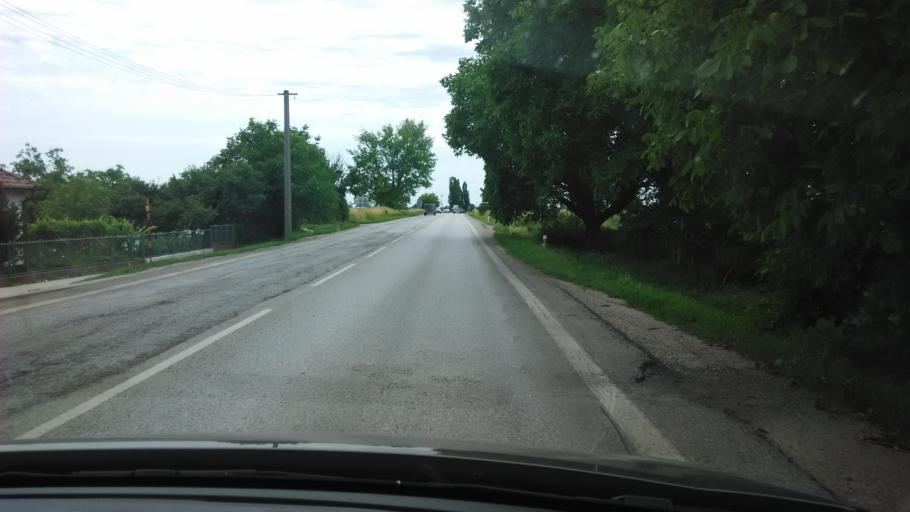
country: SK
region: Trnavsky
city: Leopoldov
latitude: 48.4369
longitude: 17.7012
